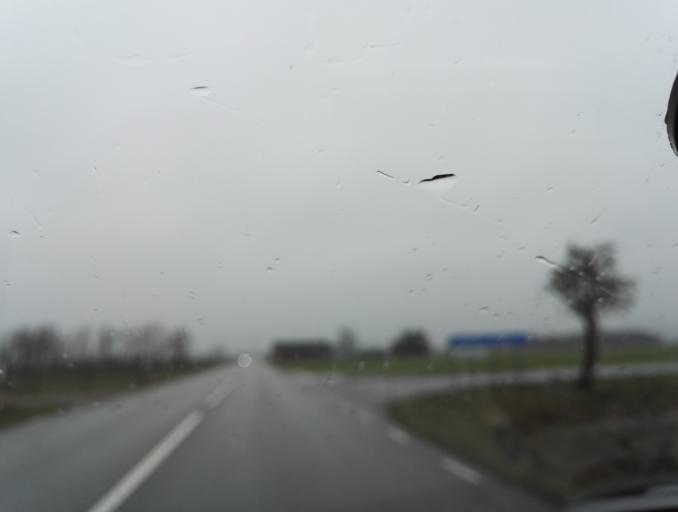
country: SE
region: Skane
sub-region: Lunds Kommun
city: Lund
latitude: 55.7484
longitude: 13.1672
